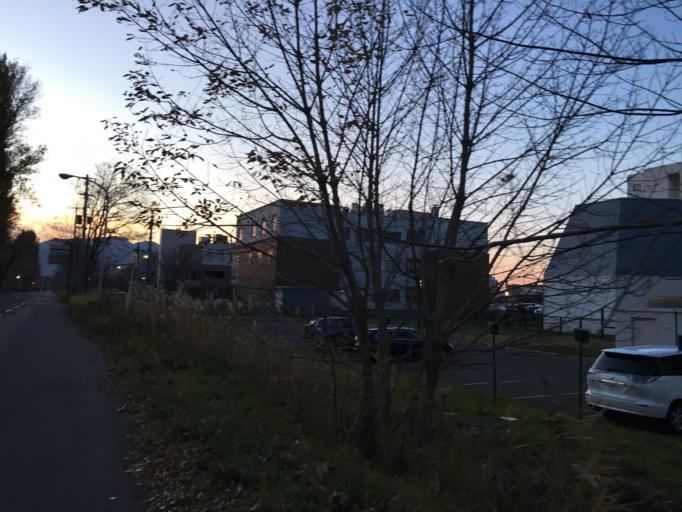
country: JP
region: Hokkaido
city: Sapporo
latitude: 43.0843
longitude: 141.3347
